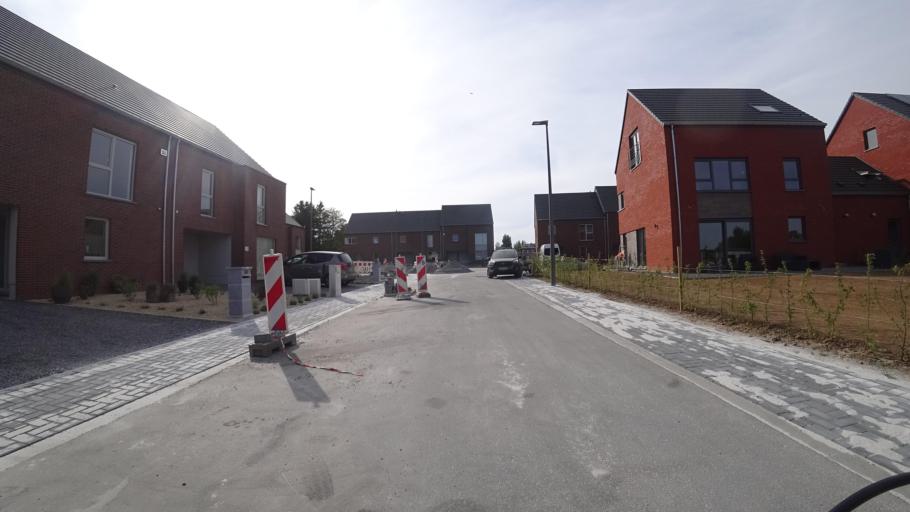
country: BE
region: Wallonia
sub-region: Province de Namur
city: Namur
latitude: 50.4645
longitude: 4.8276
